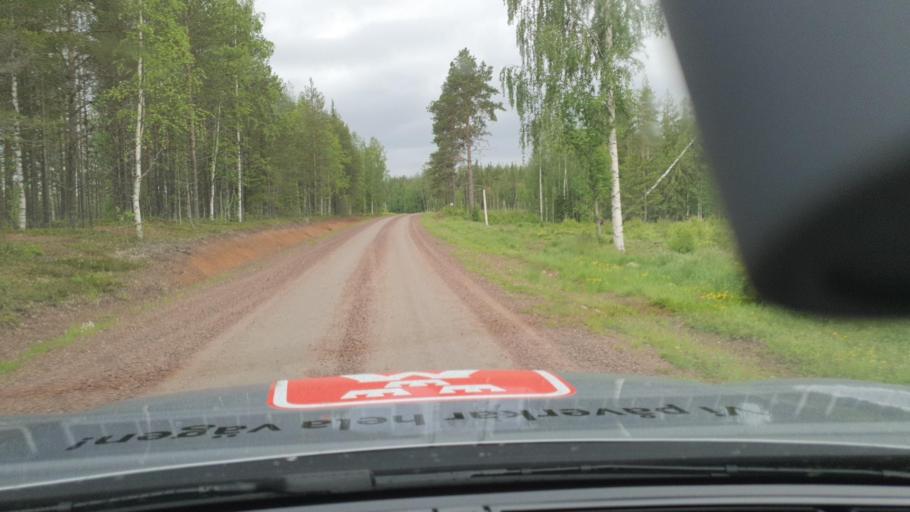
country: SE
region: Norrbotten
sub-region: Overkalix Kommun
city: OEverkalix
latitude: 66.6231
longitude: 22.7252
